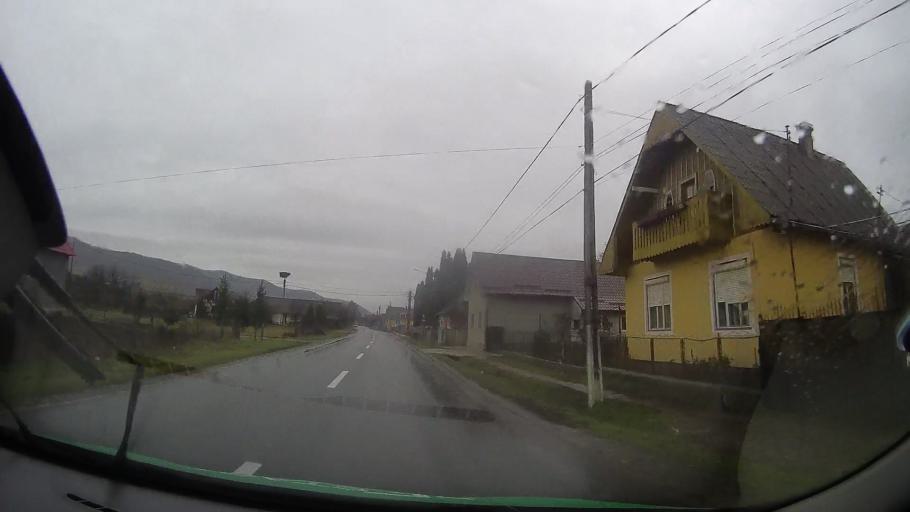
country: RO
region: Bistrita-Nasaud
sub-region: Comuna Mariselu
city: Mariselu
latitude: 47.0318
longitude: 24.4839
